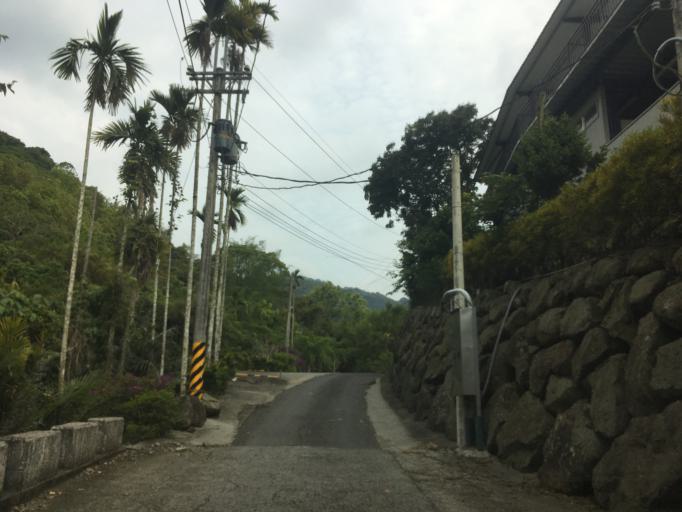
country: TW
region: Taiwan
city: Zhongxing New Village
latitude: 23.9849
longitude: 120.8141
